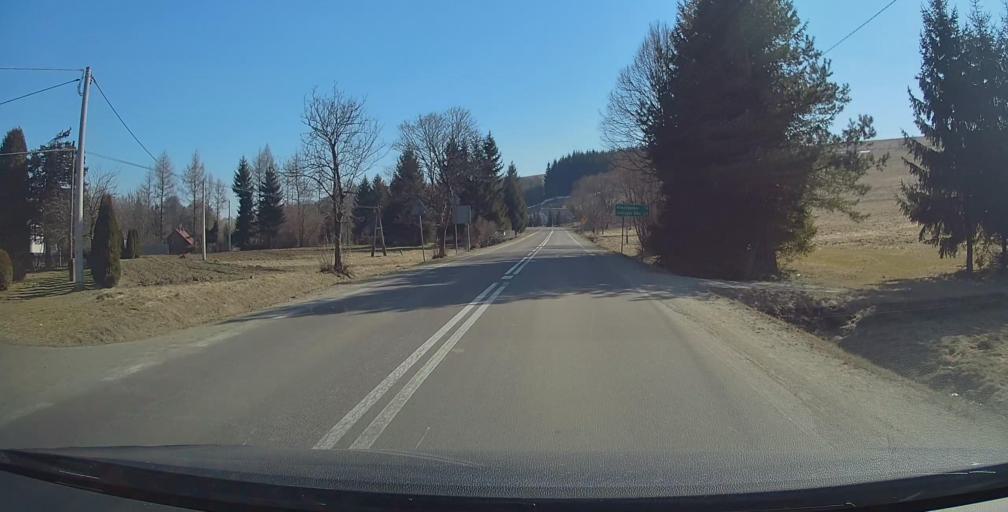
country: PL
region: Subcarpathian Voivodeship
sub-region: Powiat bieszczadzki
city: Ustrzyki Dolne
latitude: 49.5573
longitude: 22.5606
